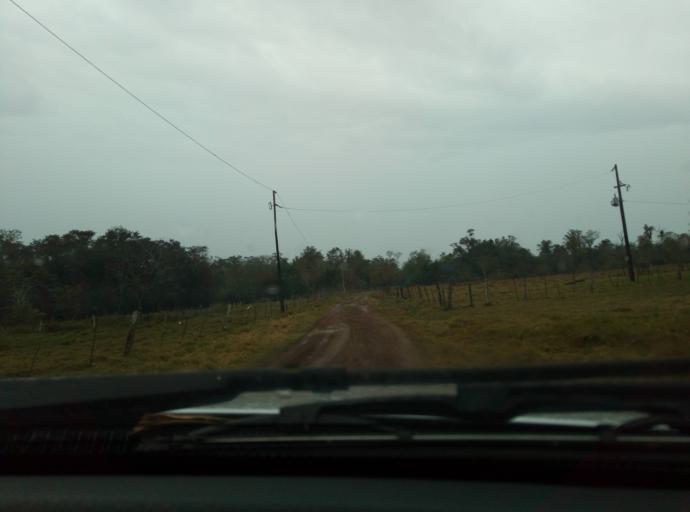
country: PY
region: Caaguazu
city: Carayao
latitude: -25.1050
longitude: -56.4155
